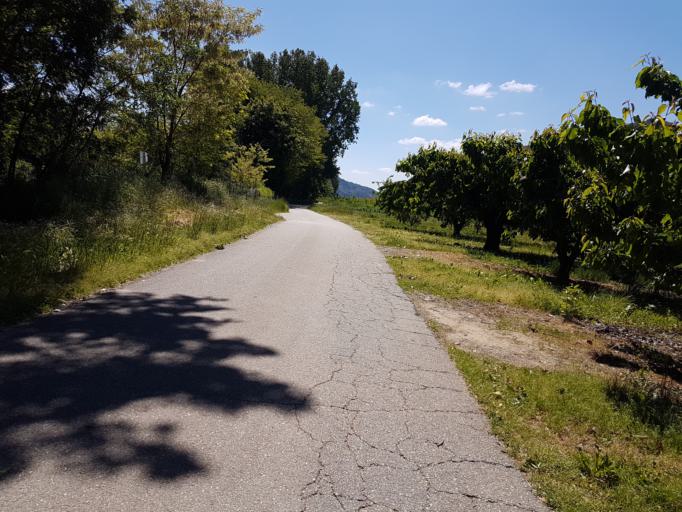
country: FR
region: Rhone-Alpes
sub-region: Departement de l'Ardeche
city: Saint-Jean-de-Muzols
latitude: 45.1162
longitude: 4.8078
